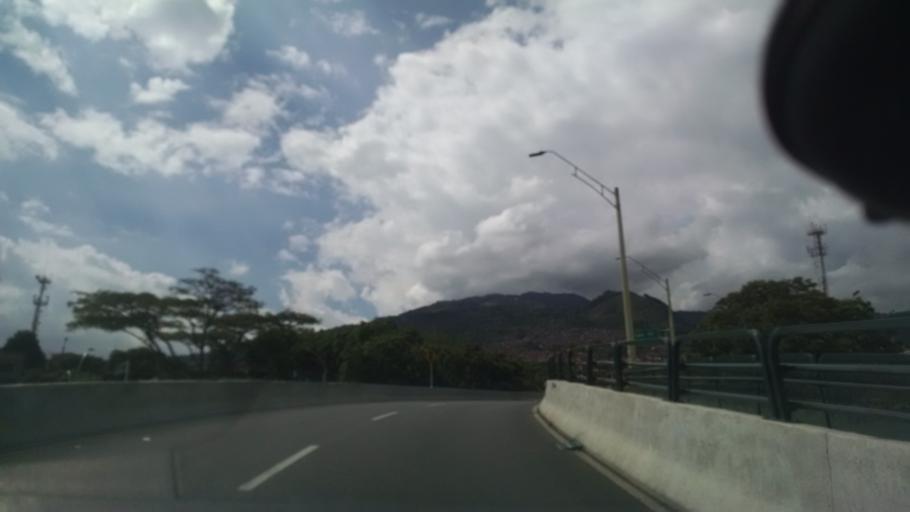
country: CO
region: Antioquia
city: Medellin
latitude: 6.2883
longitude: -75.5694
